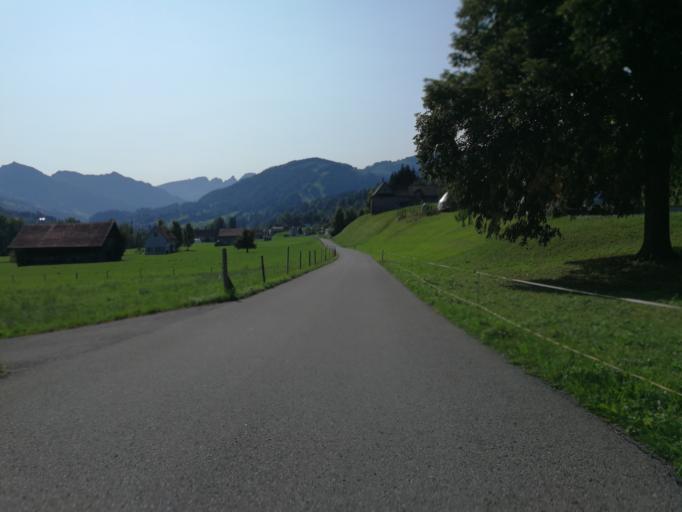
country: CH
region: Saint Gallen
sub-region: Wahlkreis Toggenburg
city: Ebnat-Kappel
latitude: 47.2714
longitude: 9.1041
